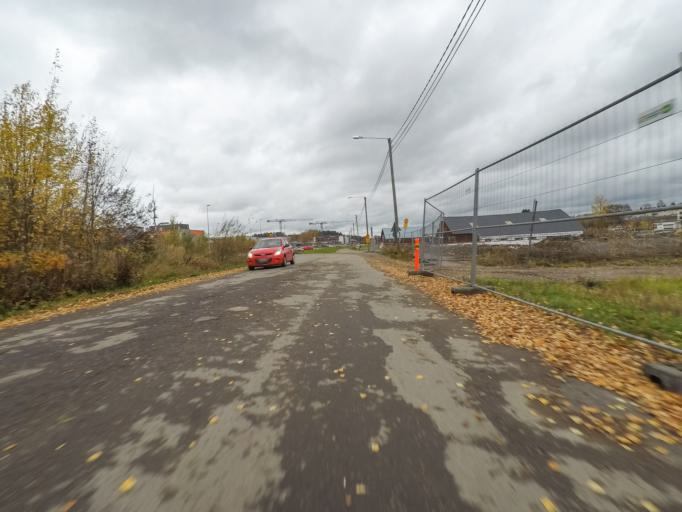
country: FI
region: Uusimaa
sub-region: Porvoo
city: Porvoo
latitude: 60.3866
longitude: 25.6608
